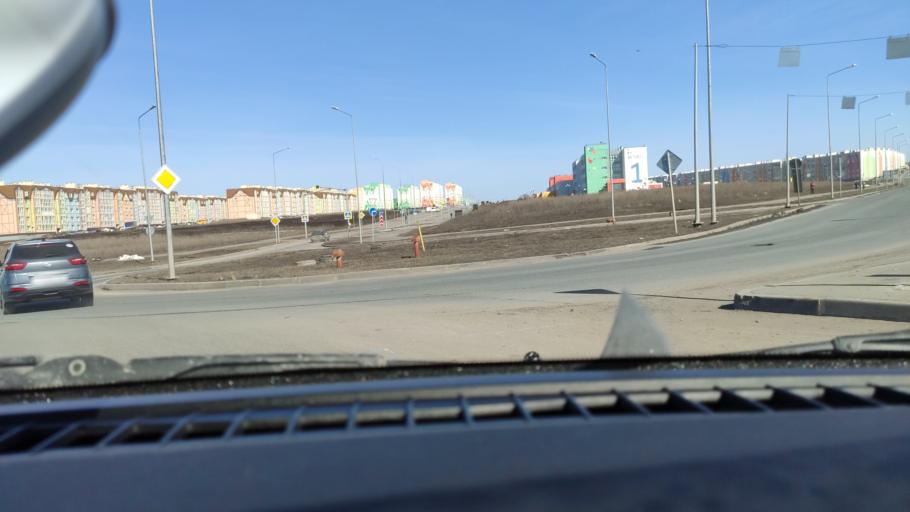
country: RU
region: Samara
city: Petra-Dubrava
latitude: 53.2940
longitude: 50.3294
